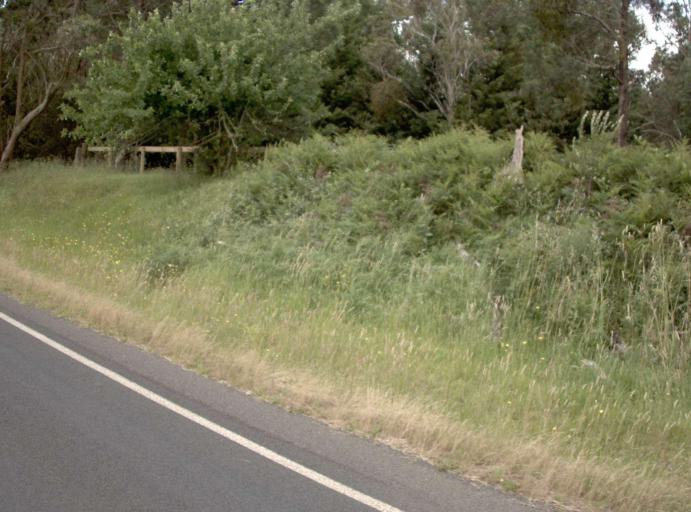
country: AU
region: Victoria
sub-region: Baw Baw
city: Warragul
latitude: -38.0850
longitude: 145.9206
